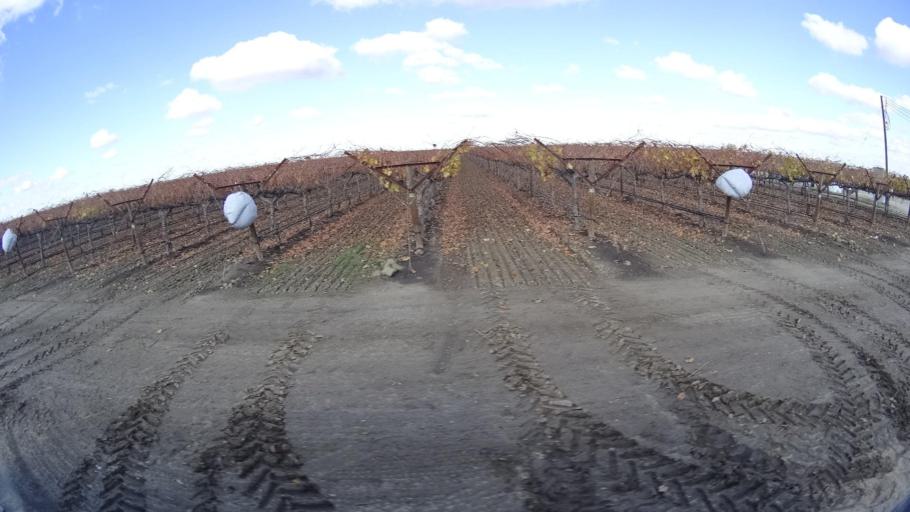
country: US
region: California
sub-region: Kern County
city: Delano
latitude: 35.7322
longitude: -119.3504
